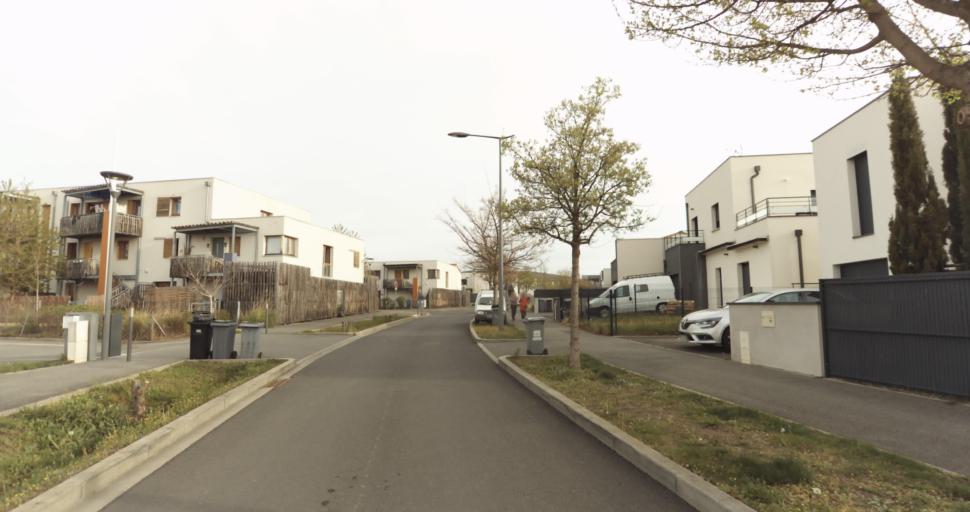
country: FR
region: Auvergne
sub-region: Departement du Puy-de-Dome
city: Cebazat
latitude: 45.8366
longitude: 3.1101
